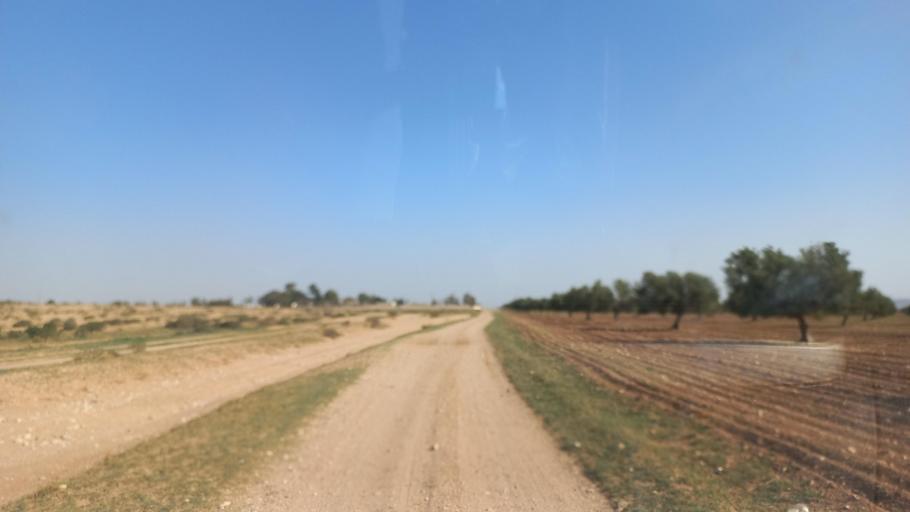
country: TN
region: Al Qasrayn
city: Kasserine
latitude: 35.2999
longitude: 9.0279
